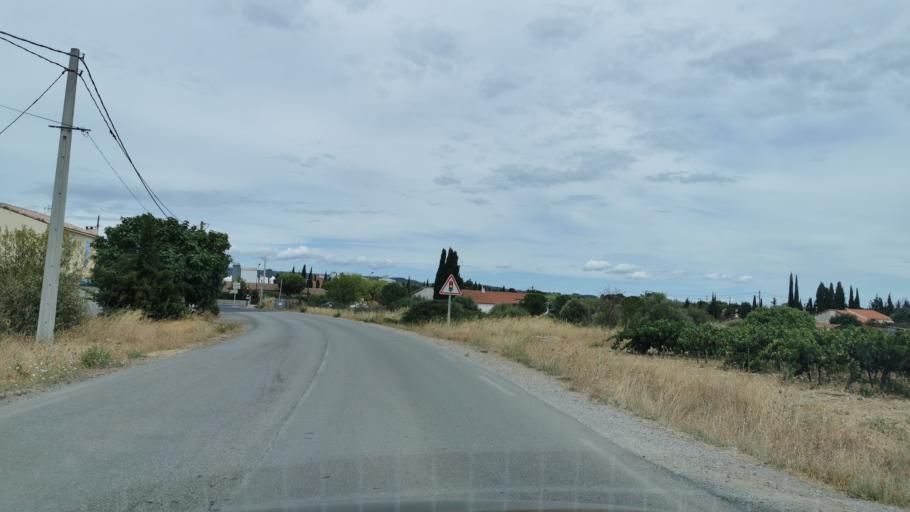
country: FR
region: Languedoc-Roussillon
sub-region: Departement de l'Aude
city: Argeliers
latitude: 43.3039
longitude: 2.9103
